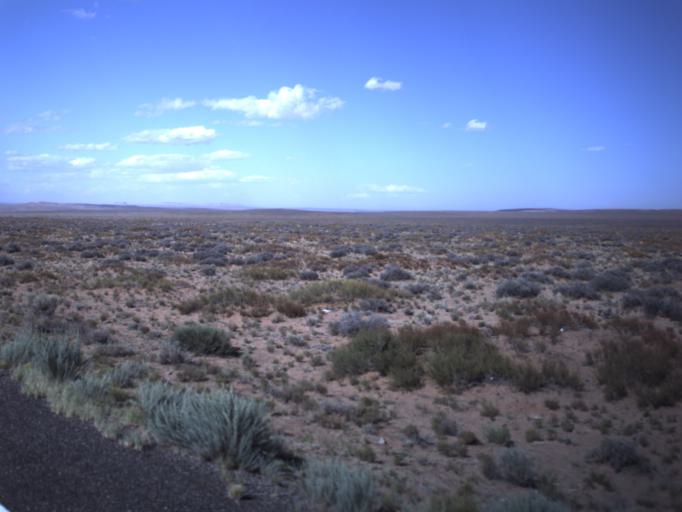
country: US
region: Utah
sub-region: Wayne County
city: Loa
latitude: 38.1673
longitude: -110.6234
